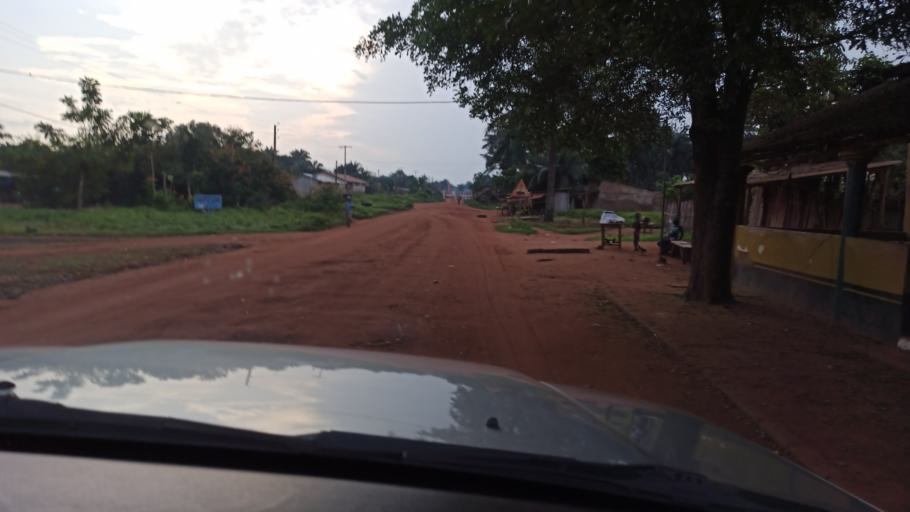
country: BJ
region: Queme
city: Porto-Novo
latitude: 6.5351
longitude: 2.6514
